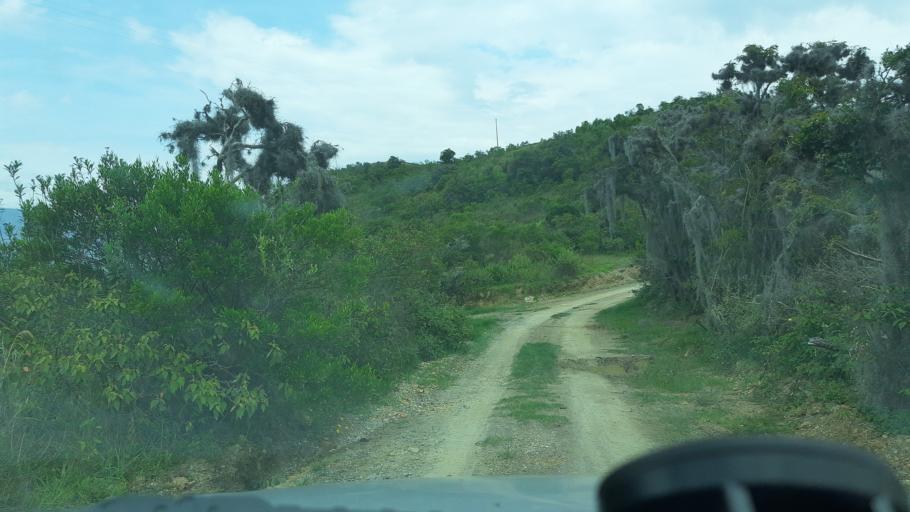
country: CO
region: Boyaca
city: Santa Sofia
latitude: 5.6995
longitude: -73.5795
